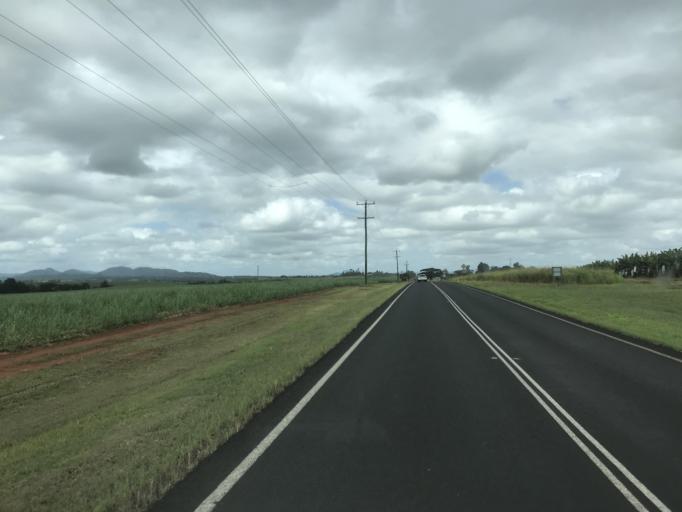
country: AU
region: Queensland
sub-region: Cassowary Coast
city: Innisfail
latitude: -17.5803
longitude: 145.9995
